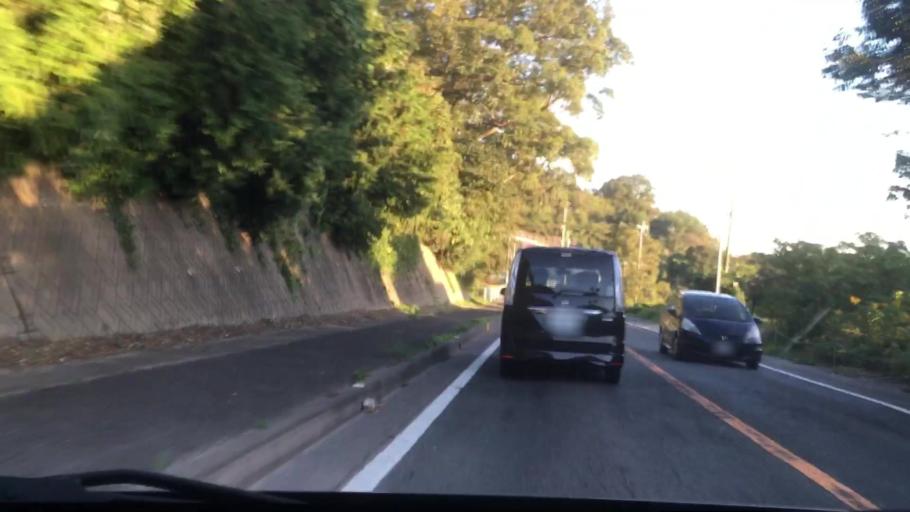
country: JP
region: Nagasaki
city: Sasebo
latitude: 33.0693
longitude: 129.7631
